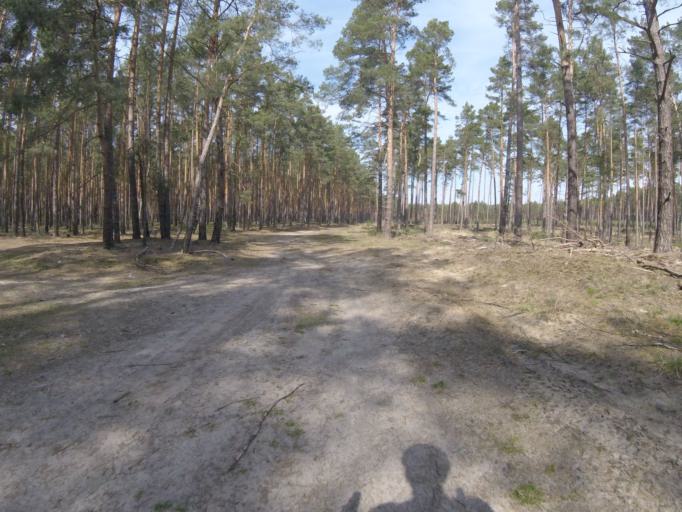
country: DE
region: Brandenburg
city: Gross Koris
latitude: 52.2051
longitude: 13.6644
